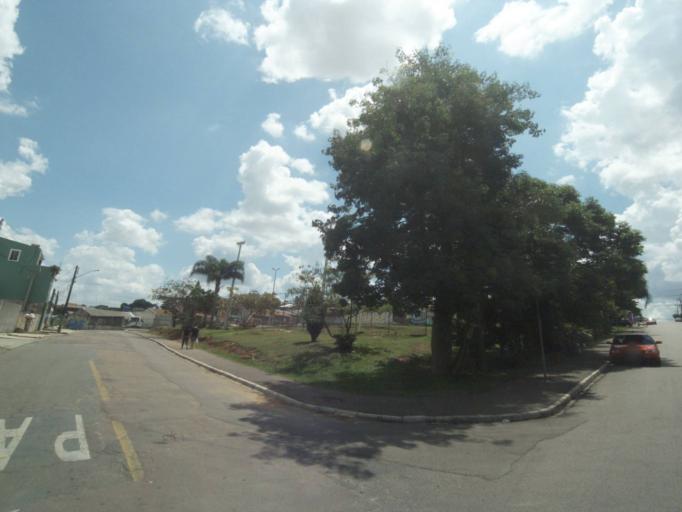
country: BR
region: Parana
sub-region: Sao Jose Dos Pinhais
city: Sao Jose dos Pinhais
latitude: -25.5302
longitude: -49.2764
